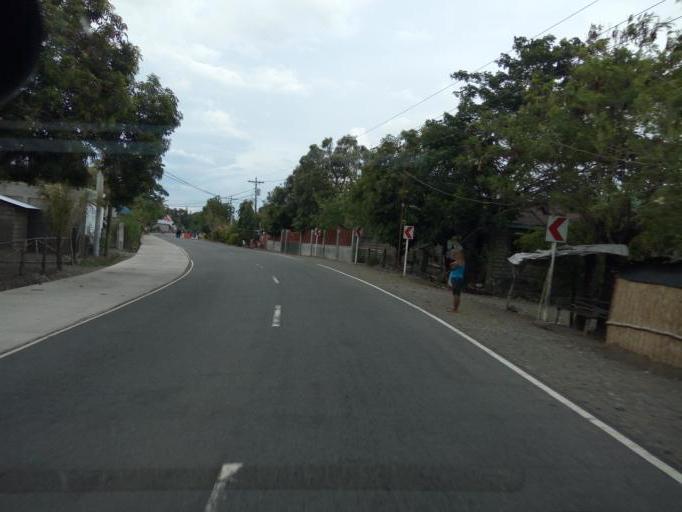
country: PH
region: Central Luzon
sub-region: Province of Nueva Ecija
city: Parista
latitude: 15.8399
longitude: 120.9360
